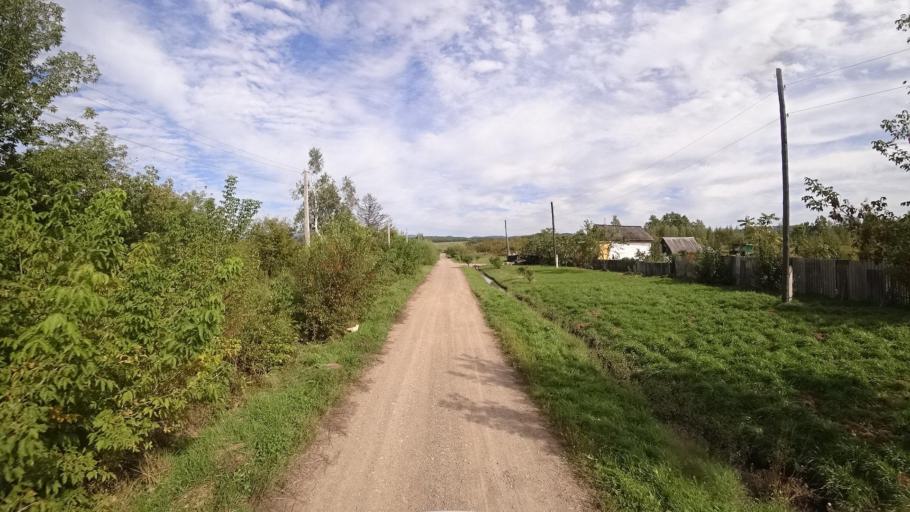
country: RU
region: Primorskiy
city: Dostoyevka
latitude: 44.3276
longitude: 133.4940
